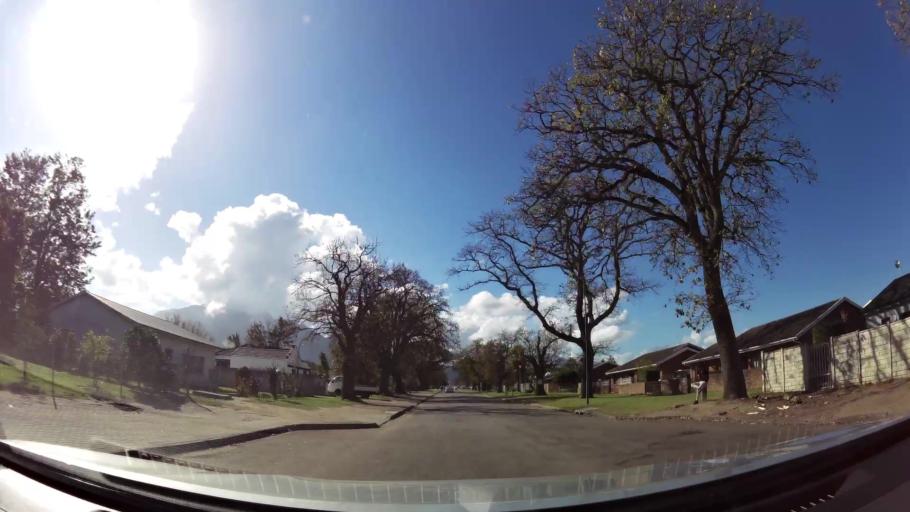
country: ZA
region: Western Cape
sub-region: Eden District Municipality
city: George
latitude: -33.9702
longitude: 22.4522
